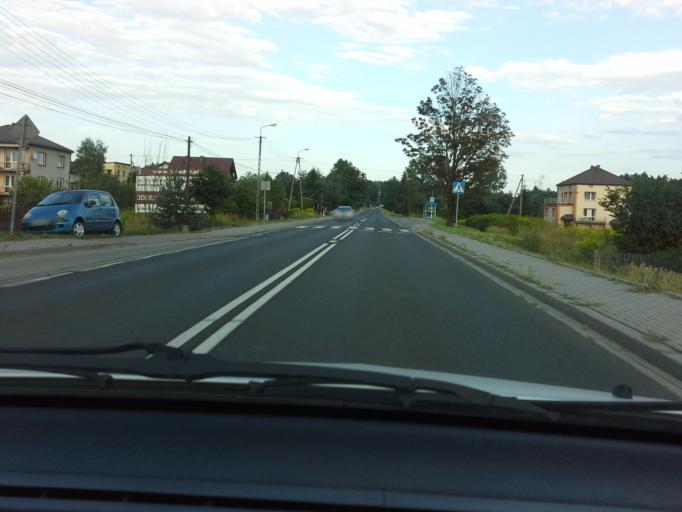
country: PL
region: Lesser Poland Voivodeship
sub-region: Powiat chrzanowski
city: Psary
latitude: 50.1425
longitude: 19.5351
